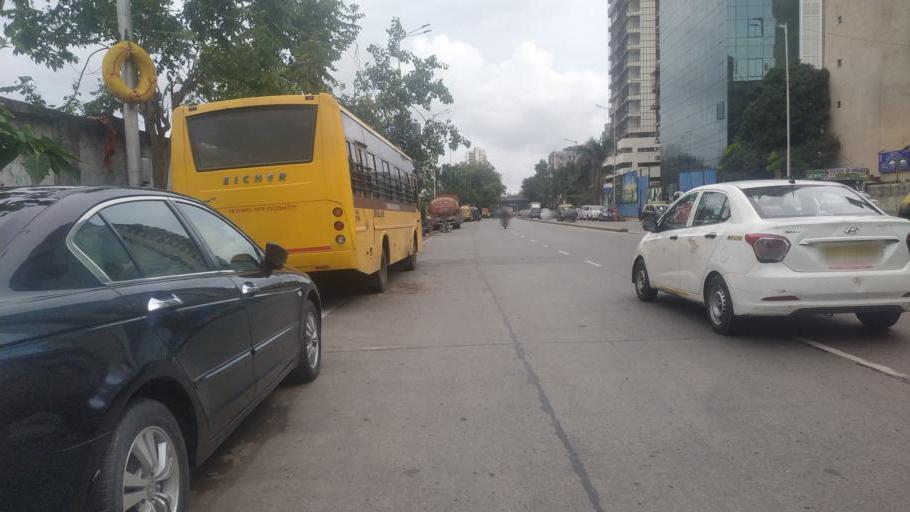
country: IN
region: Maharashtra
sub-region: Mumbai Suburban
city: Mumbai
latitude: 19.0328
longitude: 72.8477
